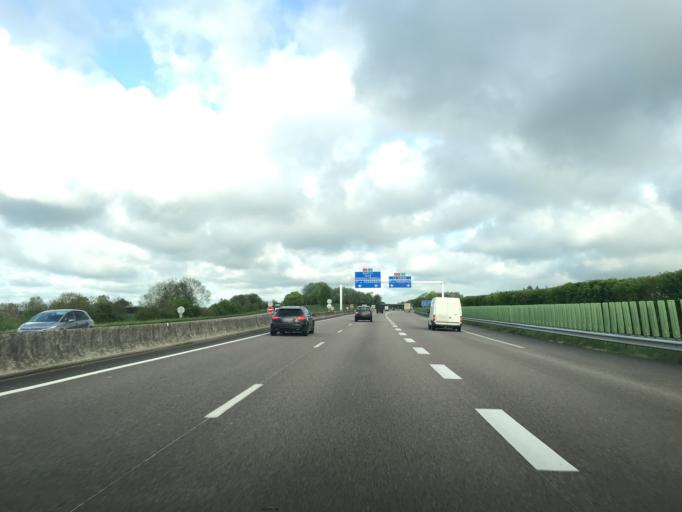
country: FR
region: Haute-Normandie
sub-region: Departement de l'Eure
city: Corneville-sur-Risle
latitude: 49.3794
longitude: 0.6156
